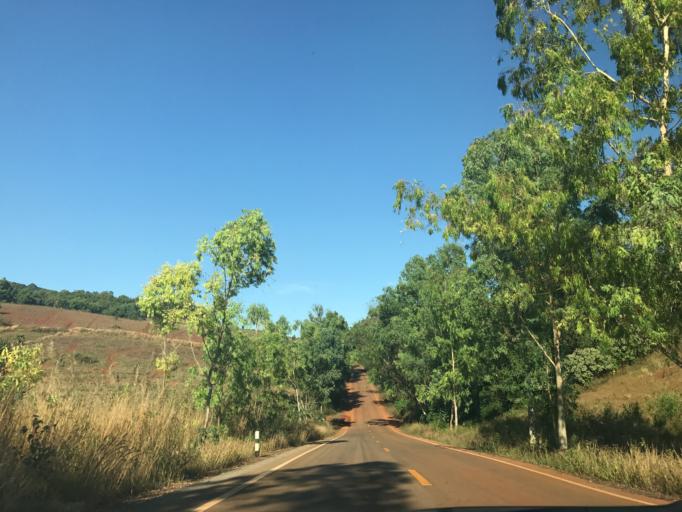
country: TH
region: Tak
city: Phop Phra
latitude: 16.5460
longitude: 98.8029
